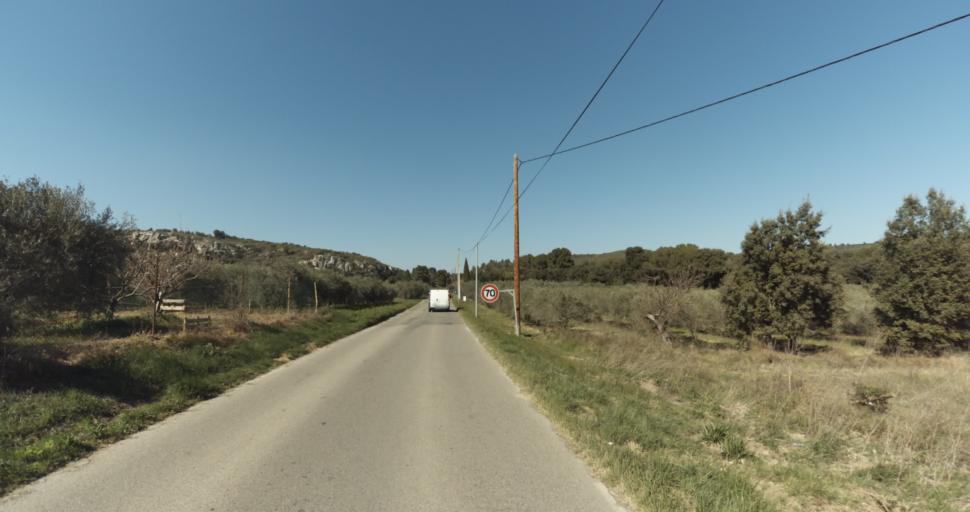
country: FR
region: Provence-Alpes-Cote d'Azur
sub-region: Departement des Bouches-du-Rhone
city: Pelissanne
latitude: 43.6502
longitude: 5.1802
